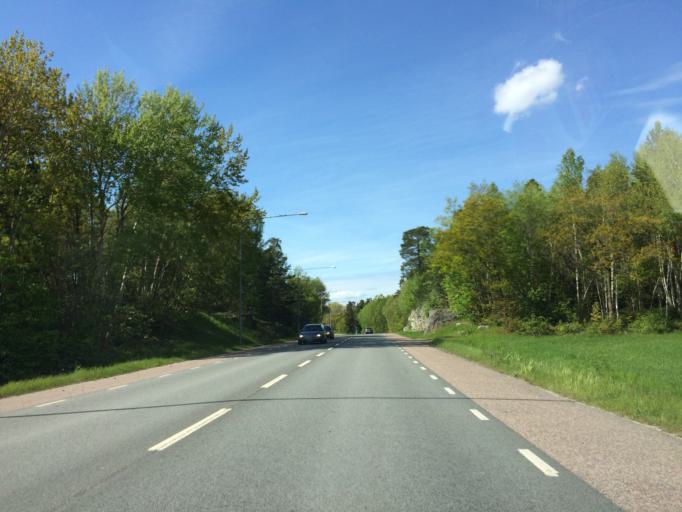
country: SE
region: Stockholm
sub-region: Norrtalje Kommun
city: Bergshamra
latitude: 59.4215
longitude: 18.0039
